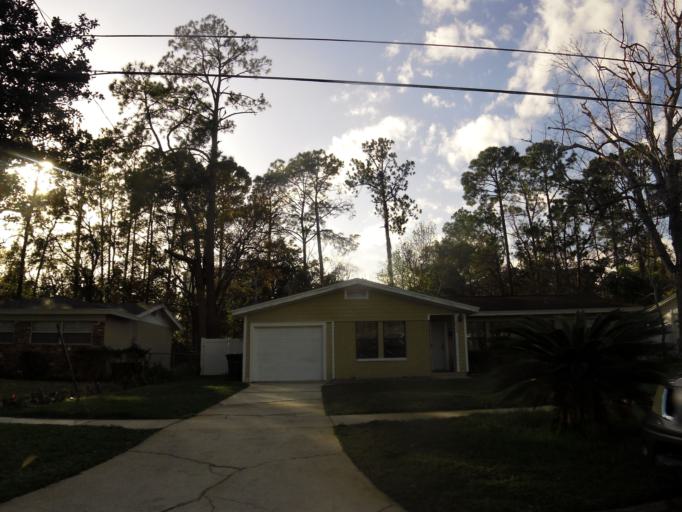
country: US
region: Florida
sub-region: Duval County
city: Jacksonville
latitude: 30.2747
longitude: -81.6014
